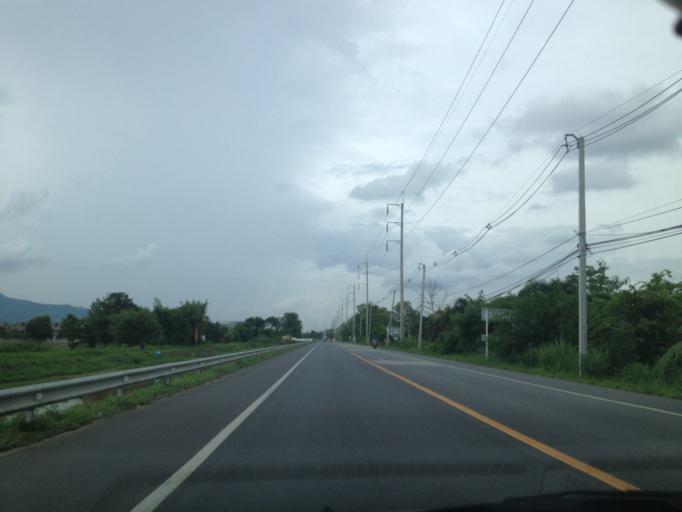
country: TH
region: Chiang Mai
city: Hang Dong
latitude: 18.7130
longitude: 98.9254
